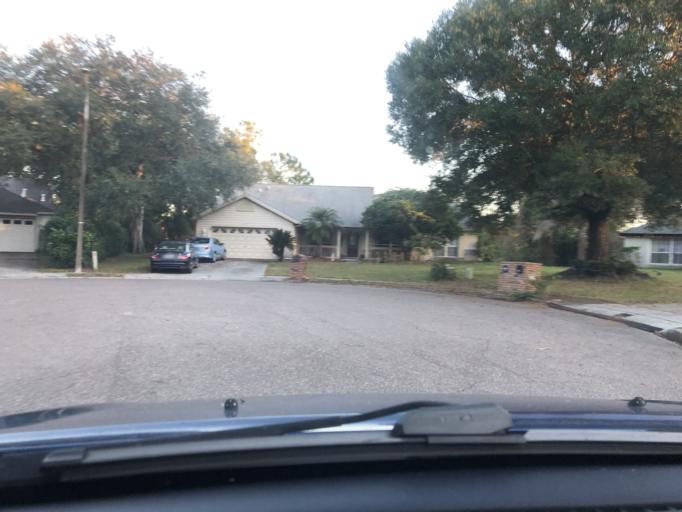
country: US
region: Florida
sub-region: Seminole County
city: Goldenrod
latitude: 28.6111
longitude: -81.2626
